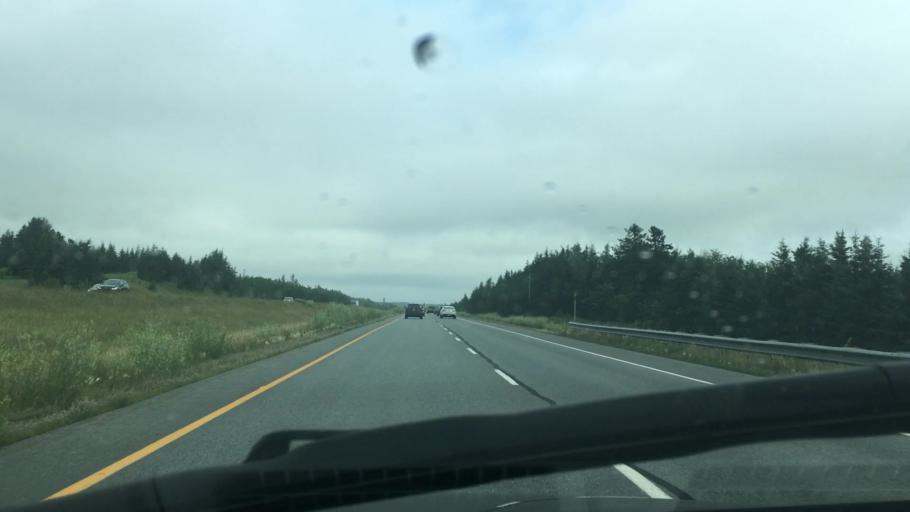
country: CA
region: Nova Scotia
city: Truro
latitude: 45.2850
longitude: -63.2979
